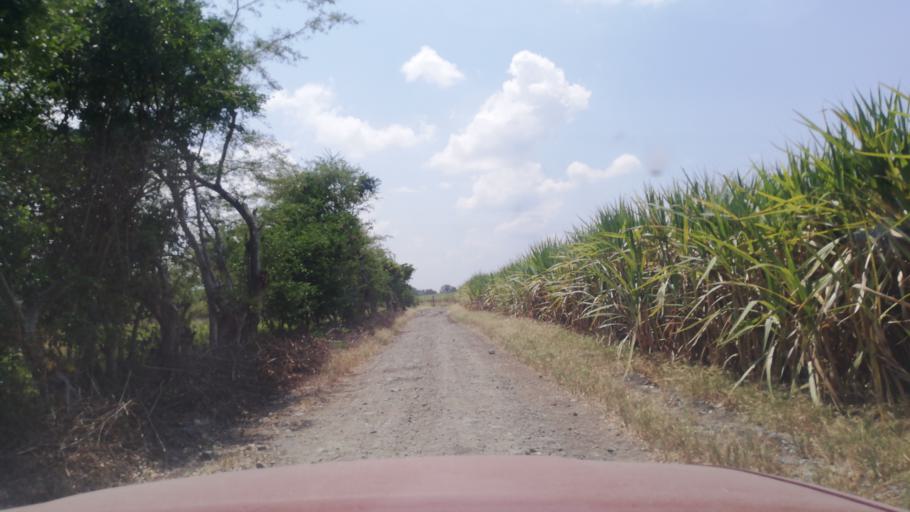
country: CO
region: Valle del Cauca
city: San Pedro
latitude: 3.9867
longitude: -76.2640
